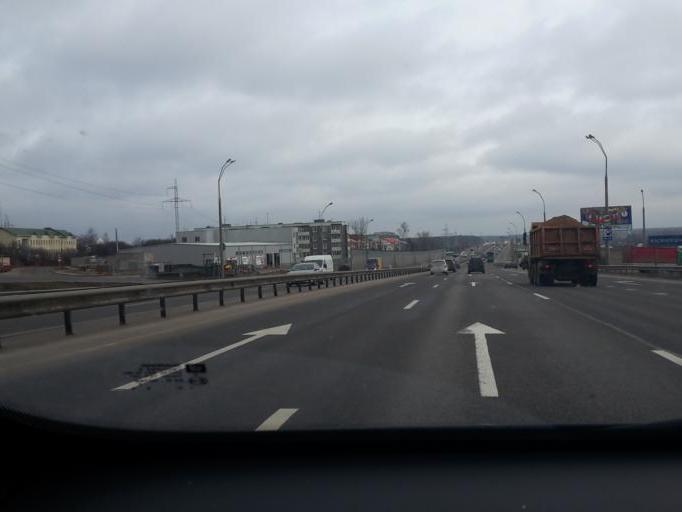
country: BY
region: Minsk
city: Zhdanovichy
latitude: 53.9364
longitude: 27.4272
